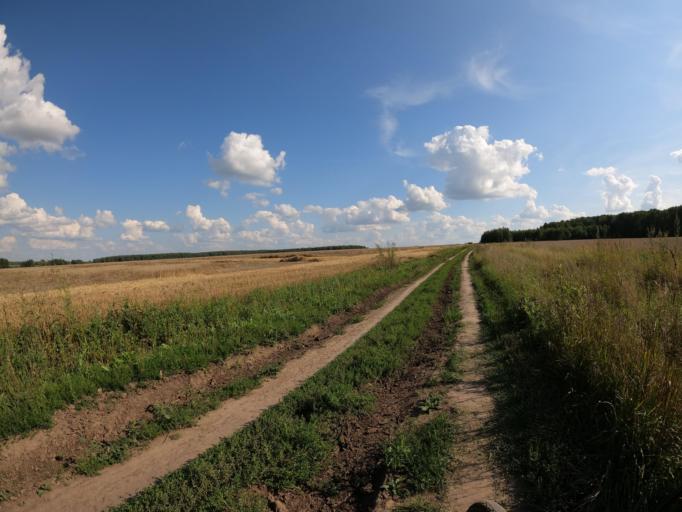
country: RU
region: Moskovskaya
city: Troitskoye
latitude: 55.2291
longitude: 38.4855
